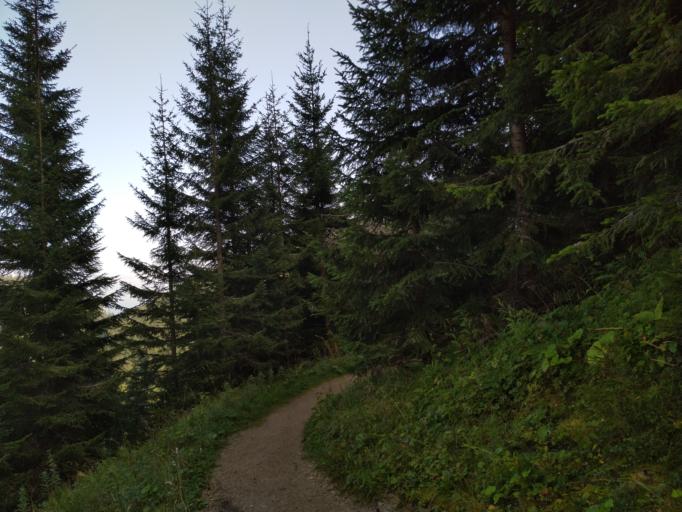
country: DE
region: Bavaria
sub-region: Upper Bavaria
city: Unterammergau
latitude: 47.5889
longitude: 11.0169
